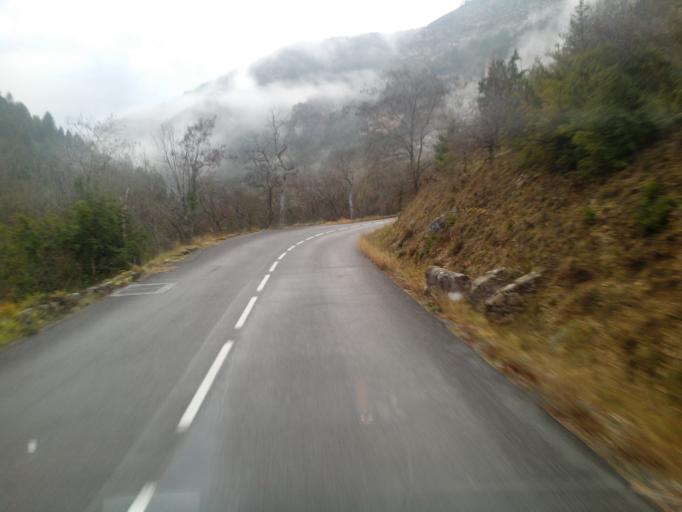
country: FR
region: Languedoc-Roussillon
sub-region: Departement de la Lozere
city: Chanac
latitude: 44.3297
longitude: 3.3534
